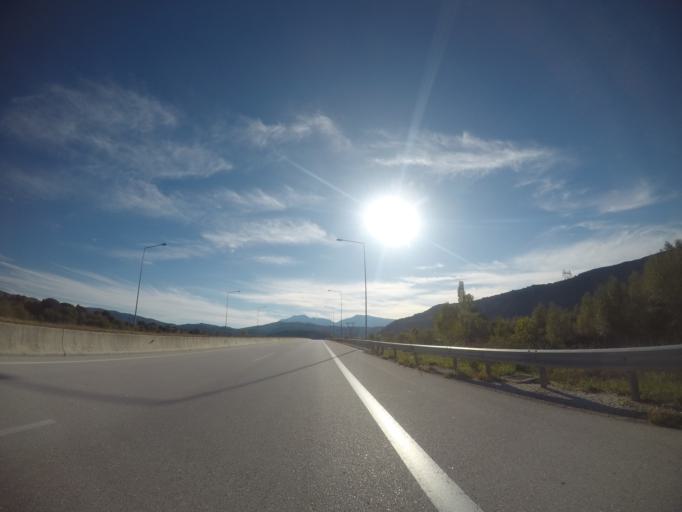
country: GR
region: Epirus
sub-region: Nomos Ioanninon
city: Koutselio
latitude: 39.6094
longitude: 20.9388
